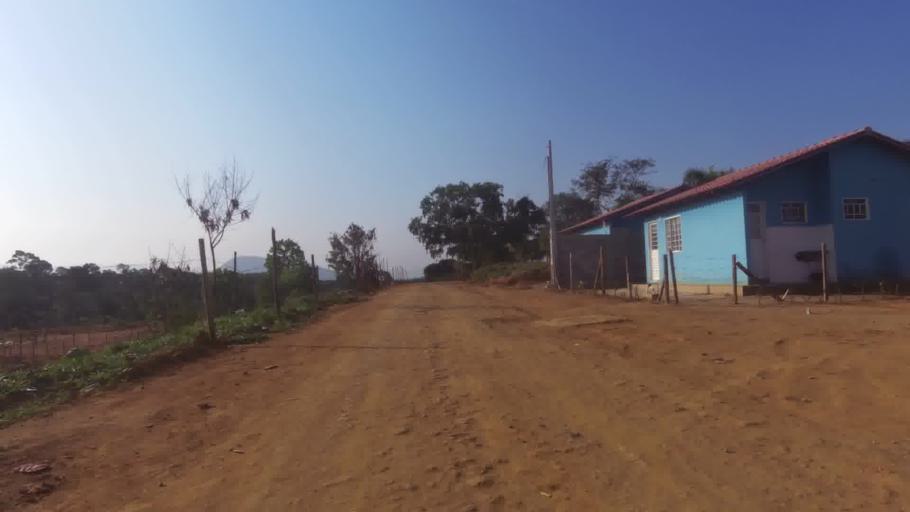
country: BR
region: Espirito Santo
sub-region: Piuma
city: Piuma
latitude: -20.8261
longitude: -40.7224
